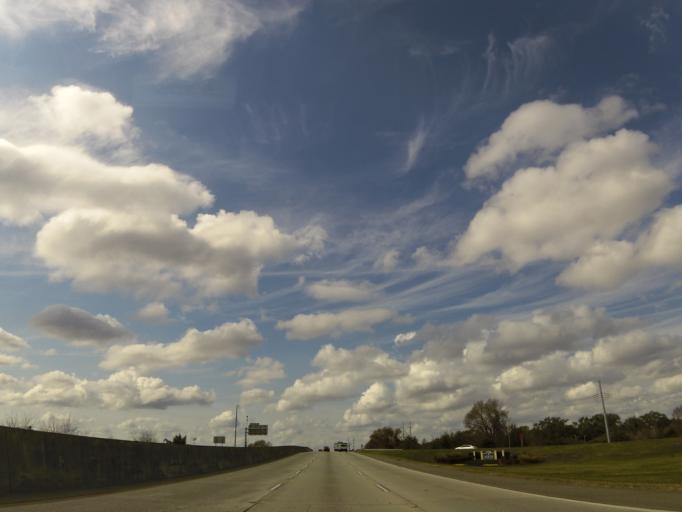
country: US
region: South Carolina
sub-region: Charleston County
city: North Charleston
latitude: 32.8429
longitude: -79.9780
